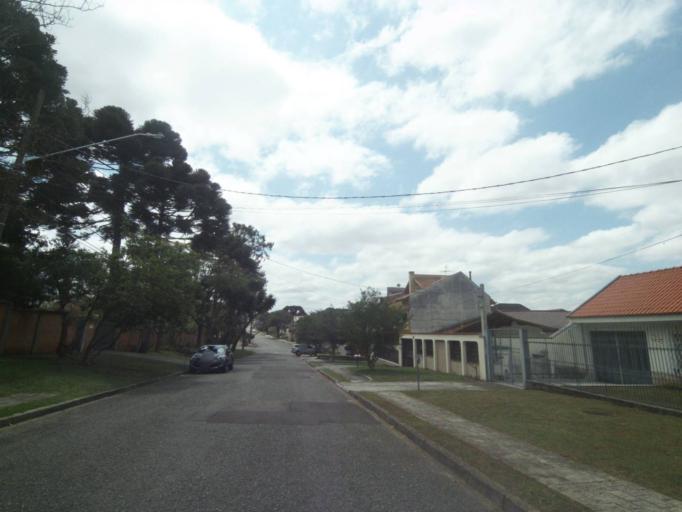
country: BR
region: Parana
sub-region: Pinhais
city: Pinhais
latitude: -25.4150
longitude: -49.2270
